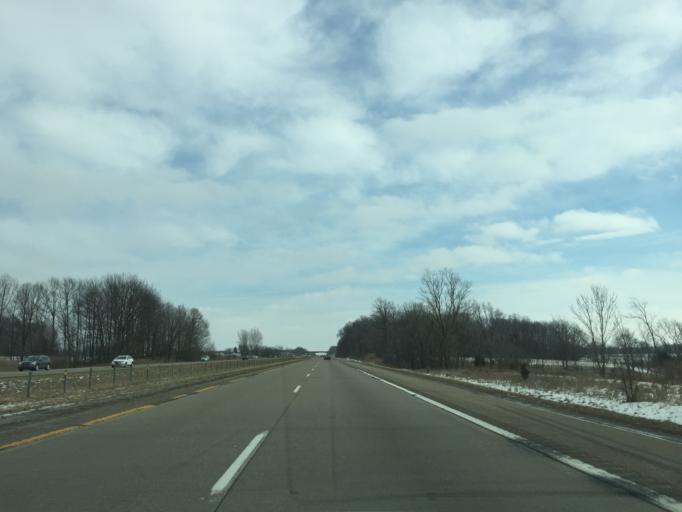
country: US
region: Michigan
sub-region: Kent County
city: Lowell
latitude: 42.8783
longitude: -85.4222
